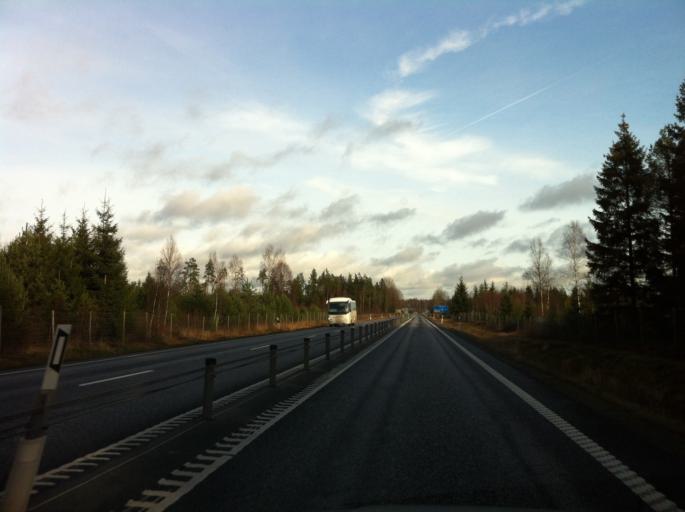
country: SE
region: Kronoberg
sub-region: Almhults Kommun
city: AElmhult
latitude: 56.6578
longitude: 14.2885
